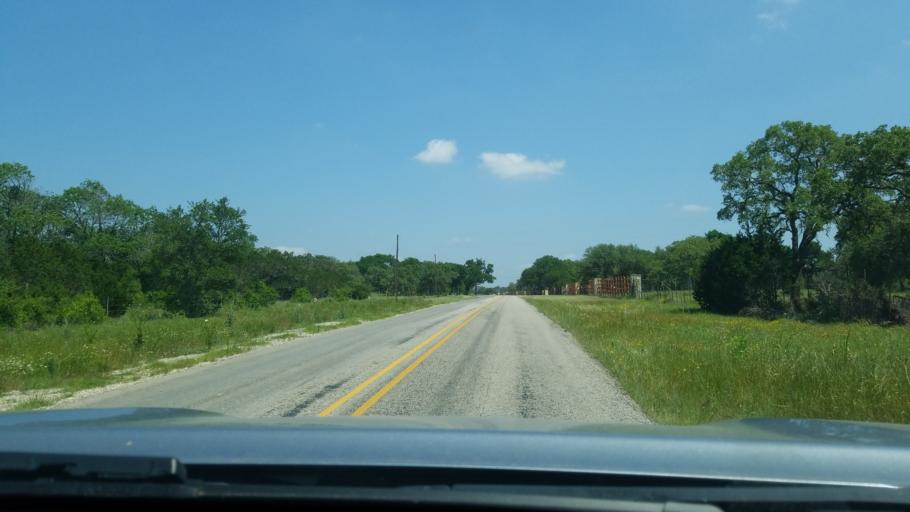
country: US
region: Texas
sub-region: Blanco County
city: Blanco
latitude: 29.9771
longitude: -98.5436
